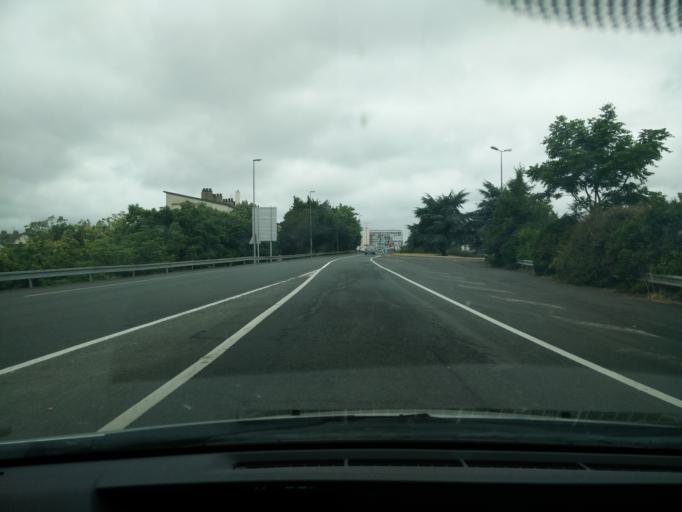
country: FR
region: Pays de la Loire
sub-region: Departement de Maine-et-Loire
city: Angers
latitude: 47.4671
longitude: -0.5272
